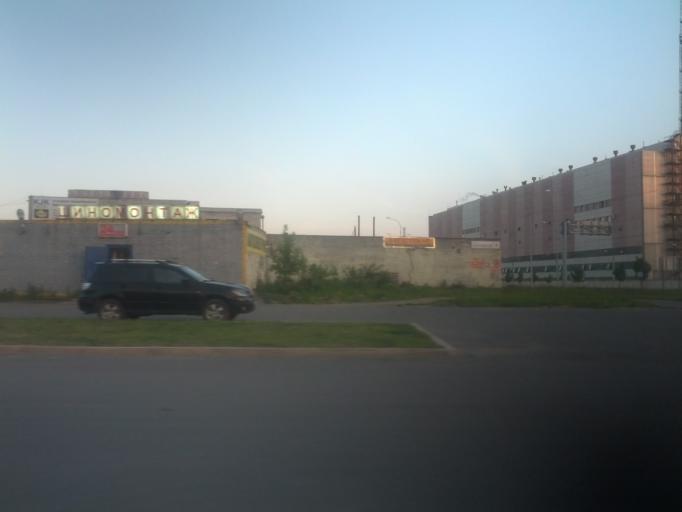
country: RU
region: St.-Petersburg
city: Staraya Derevnya
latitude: 59.9965
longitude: 30.2449
